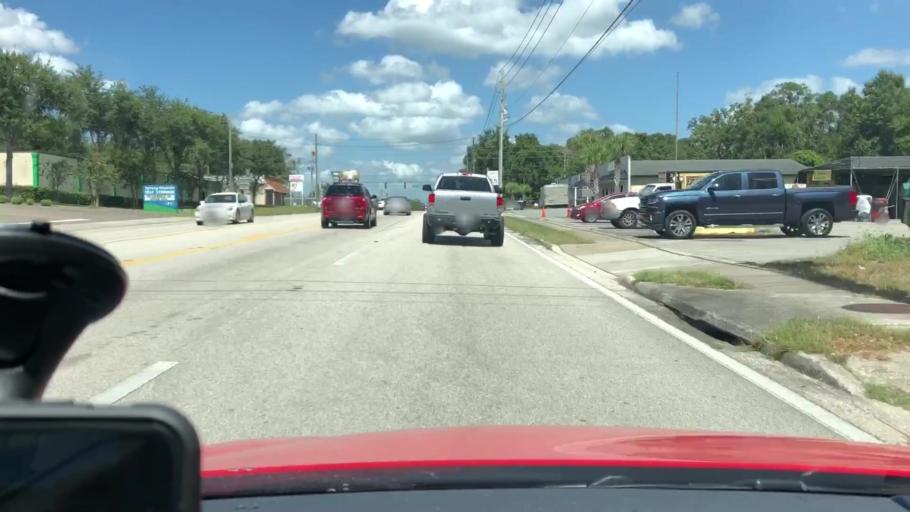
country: US
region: Florida
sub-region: Volusia County
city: West DeLand
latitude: 29.0192
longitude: -81.3239
